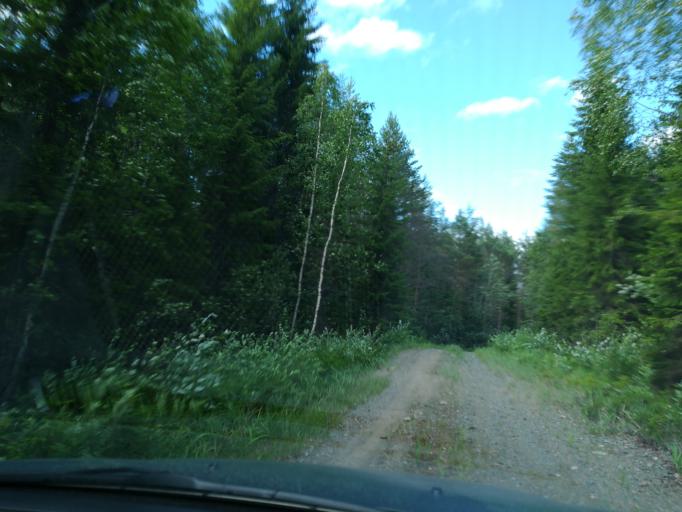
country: FI
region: South Karelia
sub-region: Lappeenranta
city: Savitaipale
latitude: 61.3010
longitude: 27.6178
